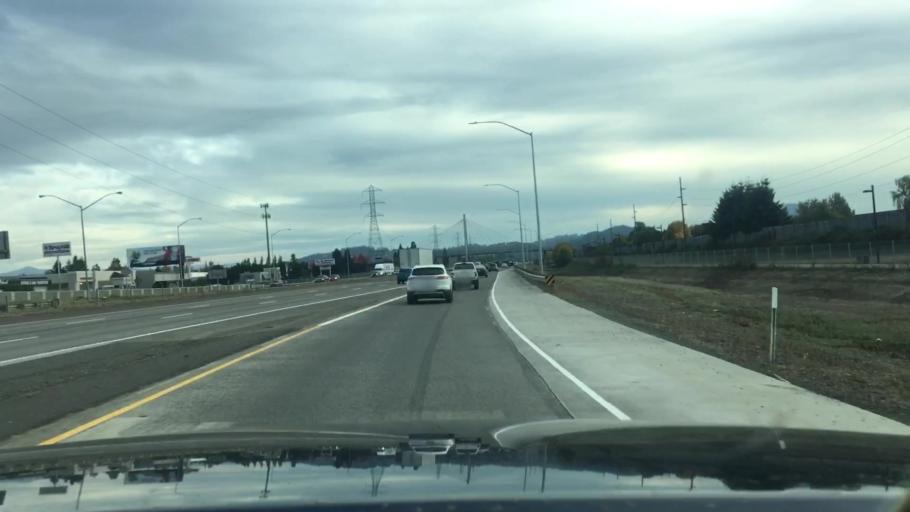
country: US
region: Oregon
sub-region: Lane County
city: Springfield
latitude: 44.0811
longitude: -123.0474
